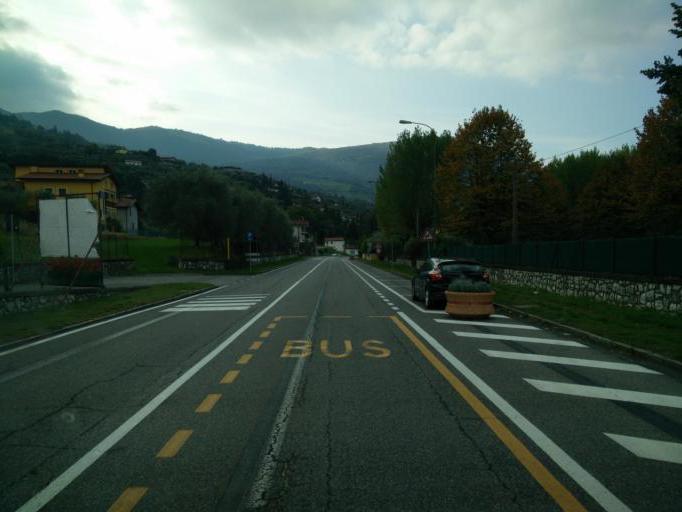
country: IT
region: Lombardy
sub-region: Provincia di Brescia
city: Sale Marasino
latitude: 45.7034
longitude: 10.1083
